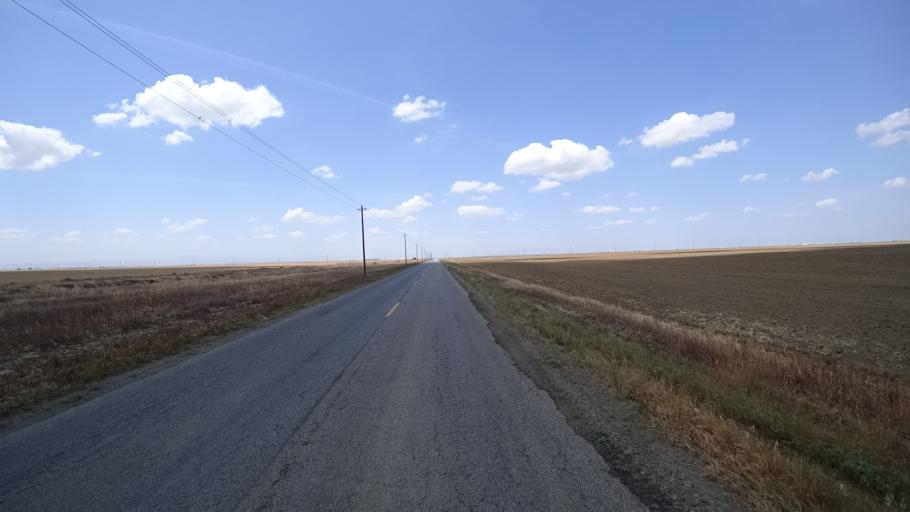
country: US
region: California
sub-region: Kings County
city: Stratford
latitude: 36.1894
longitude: -119.8970
